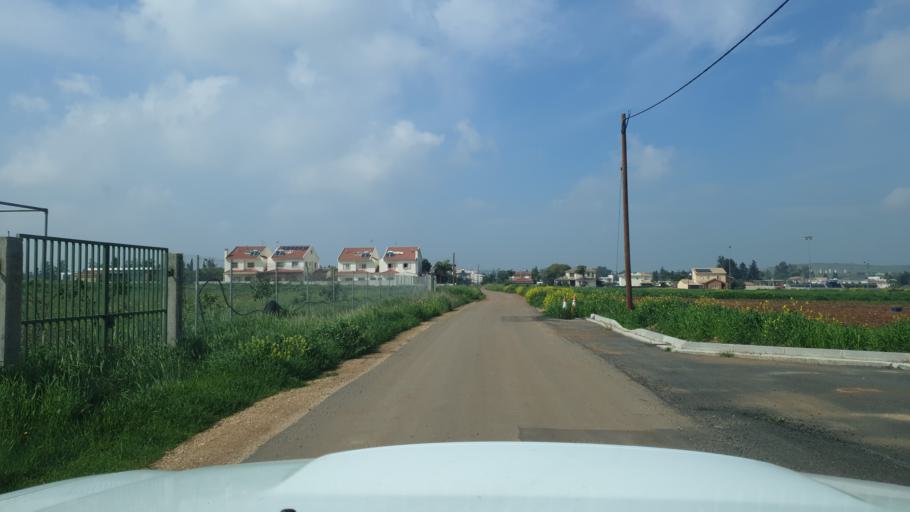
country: CY
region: Lefkosia
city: Kato Deftera
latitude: 35.0812
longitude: 33.2914
